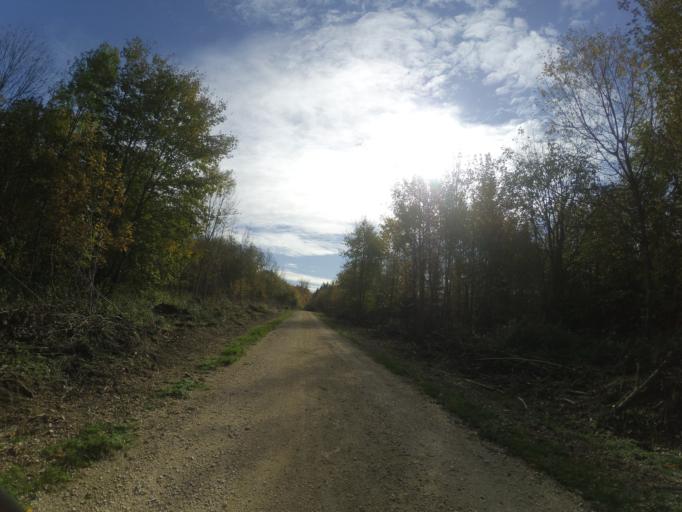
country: DE
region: Baden-Wuerttemberg
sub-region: Tuebingen Region
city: Lonsee
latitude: 48.5957
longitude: 9.9456
